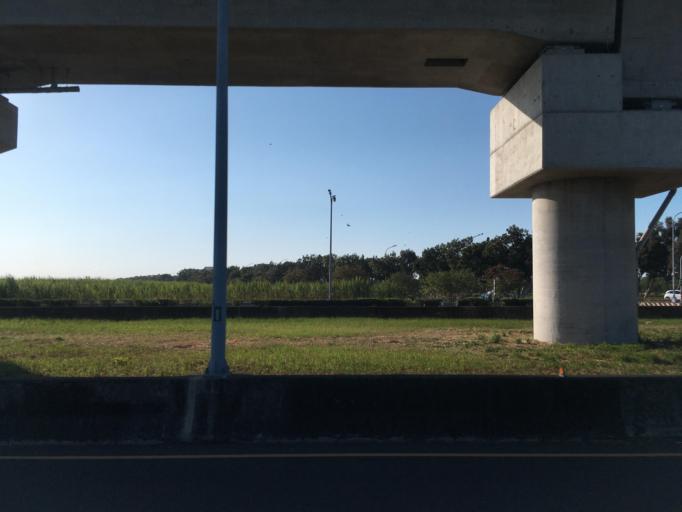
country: TW
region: Taiwan
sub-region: Chiayi
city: Taibao
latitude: 23.4515
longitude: 120.3236
